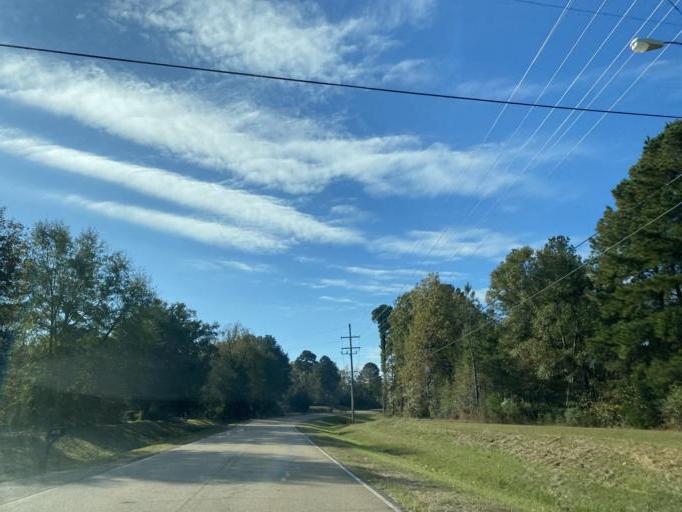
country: US
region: Mississippi
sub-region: Madison County
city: Madison
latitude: 32.4821
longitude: -90.1769
